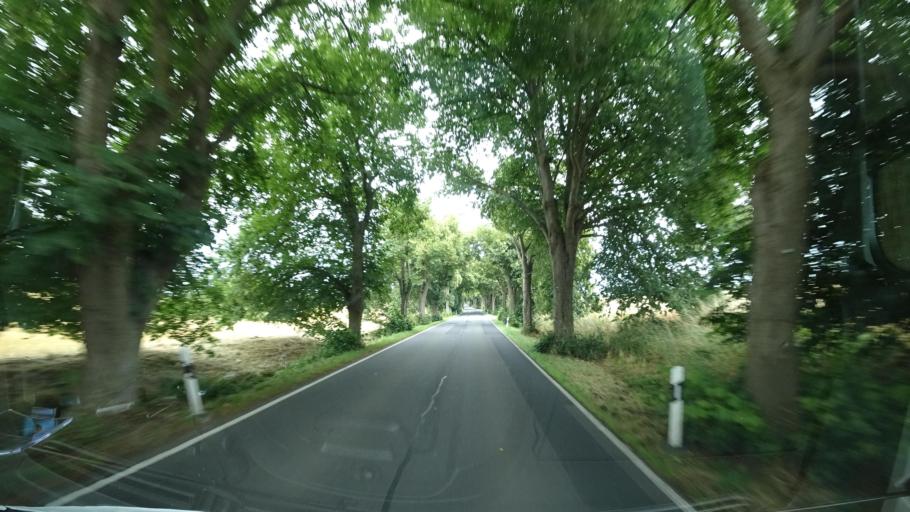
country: DE
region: Mecklenburg-Vorpommern
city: Poseritz
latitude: 54.3031
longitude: 13.2463
